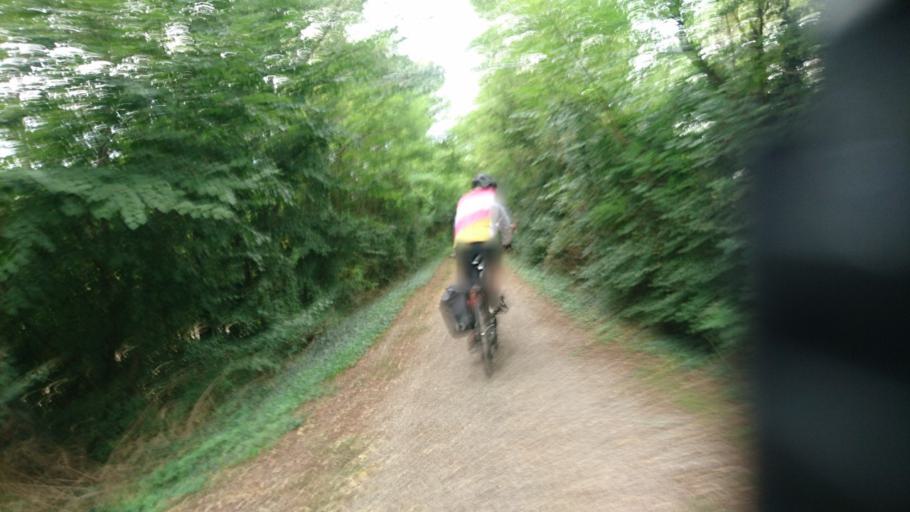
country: IT
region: Veneto
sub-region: Provincia di Vicenza
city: Zermeghedo
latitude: 45.4711
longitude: 11.3857
